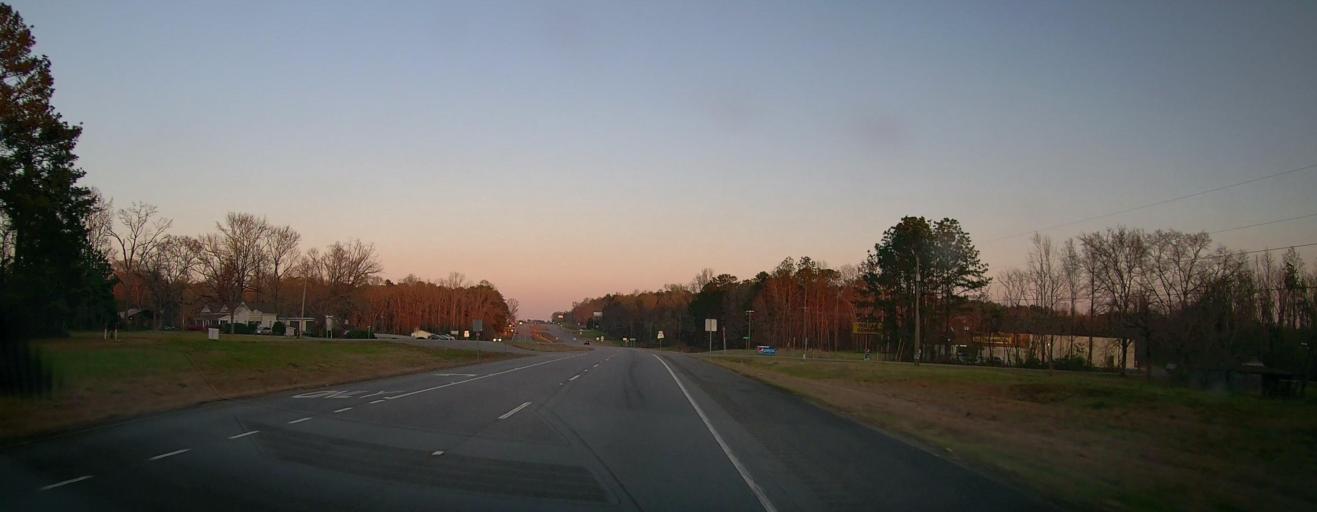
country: US
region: Alabama
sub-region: Coosa County
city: Goodwater
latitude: 32.9758
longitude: -86.0401
